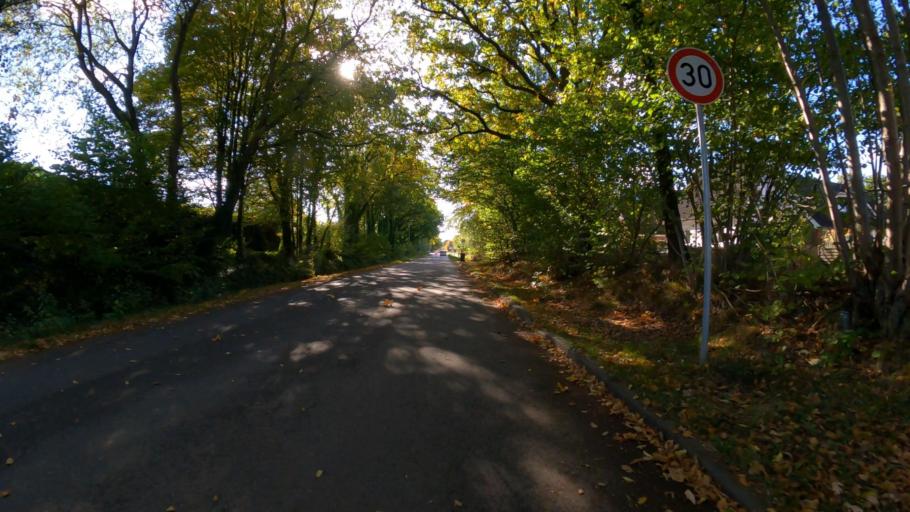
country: DE
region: Schleswig-Holstein
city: Grosshansdorf
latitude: 53.6510
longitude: 10.2542
